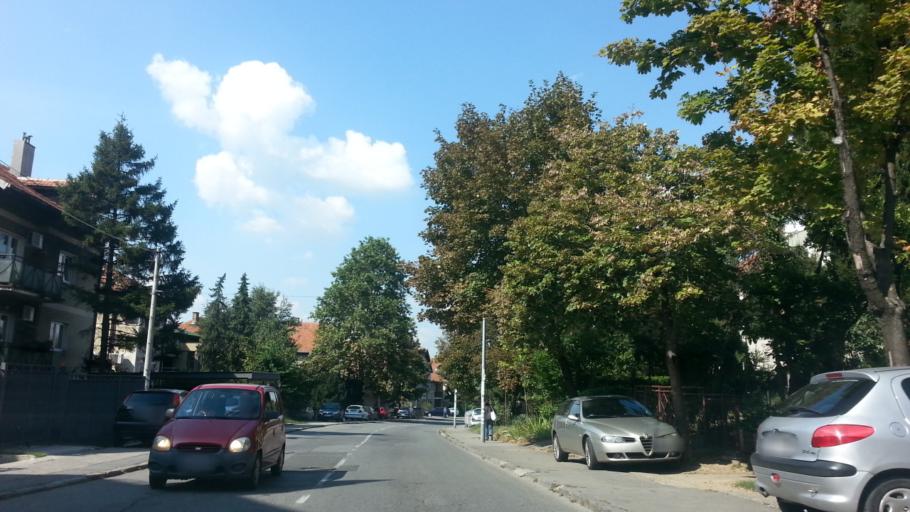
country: RS
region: Central Serbia
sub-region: Belgrade
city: Cukarica
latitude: 44.7683
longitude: 20.4195
